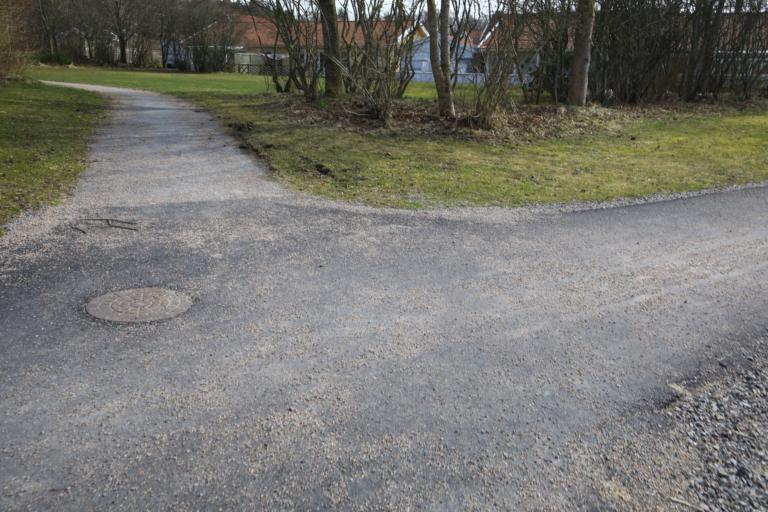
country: SE
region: Halland
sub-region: Varbergs Kommun
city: Varberg
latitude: 57.1405
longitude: 12.2839
